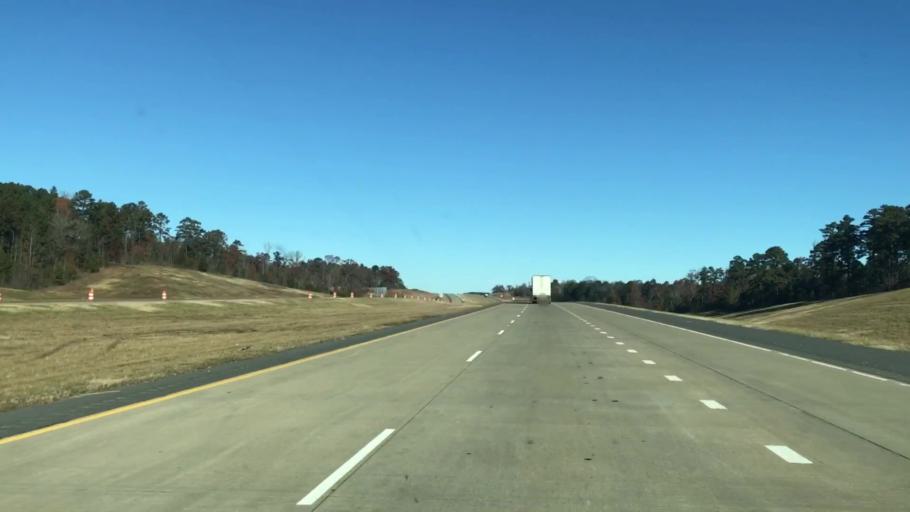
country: US
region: Louisiana
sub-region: Caddo Parish
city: Vivian
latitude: 32.9475
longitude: -93.8984
